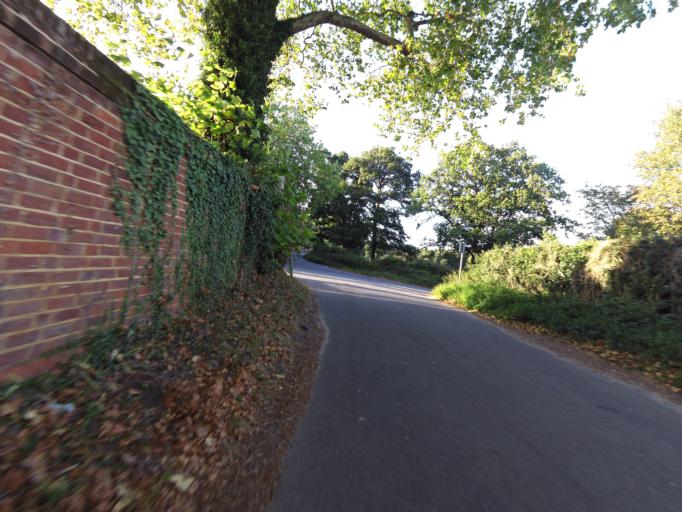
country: GB
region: England
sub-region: Suffolk
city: Kesgrave
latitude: 52.0106
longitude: 1.2306
